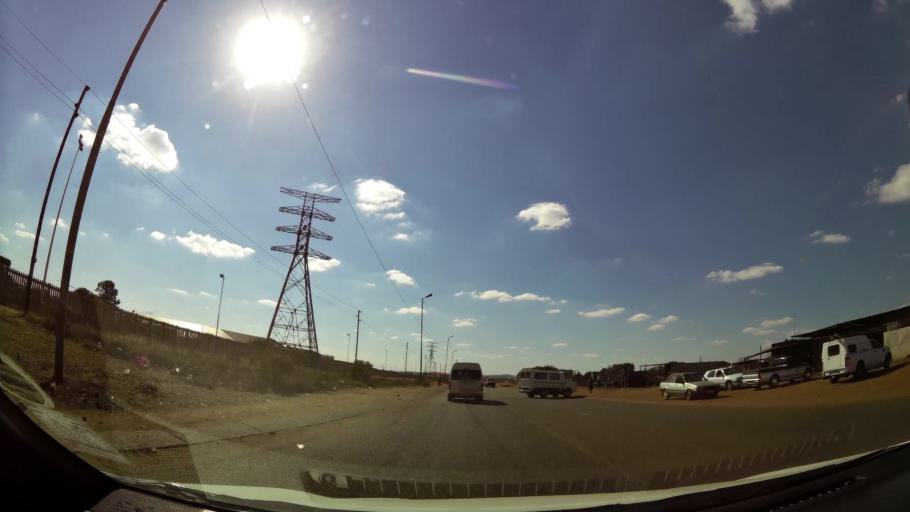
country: ZA
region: Gauteng
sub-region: City of Tshwane Metropolitan Municipality
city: Cullinan
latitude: -25.7224
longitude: 28.4008
